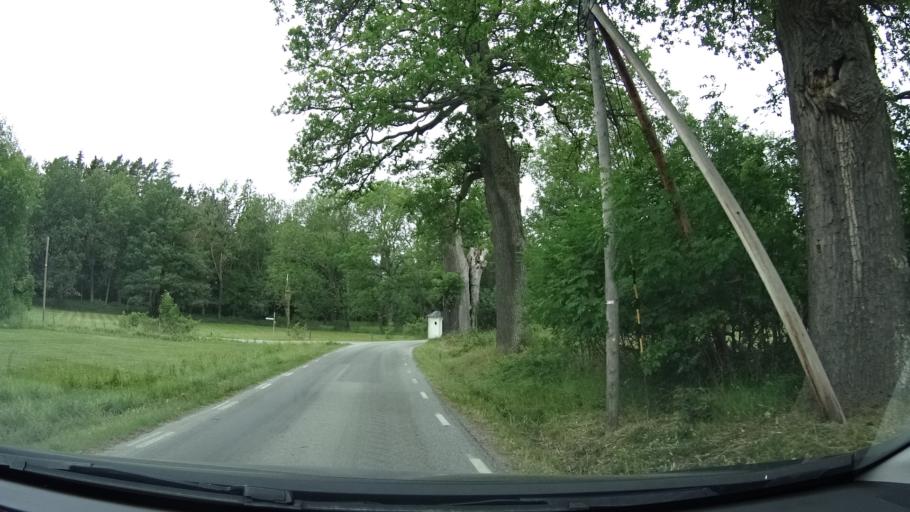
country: SE
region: Stockholm
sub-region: Varmdo Kommun
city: Mortnas
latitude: 59.3793
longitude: 18.4600
